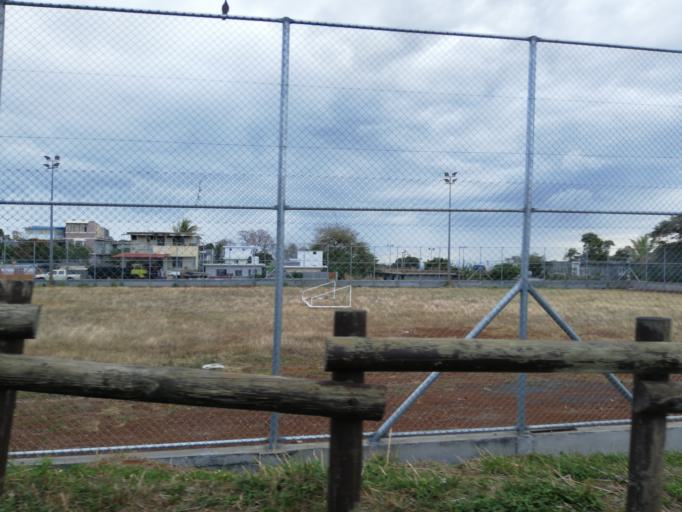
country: MU
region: Black River
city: Petite Riviere
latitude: -20.2117
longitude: 57.4662
